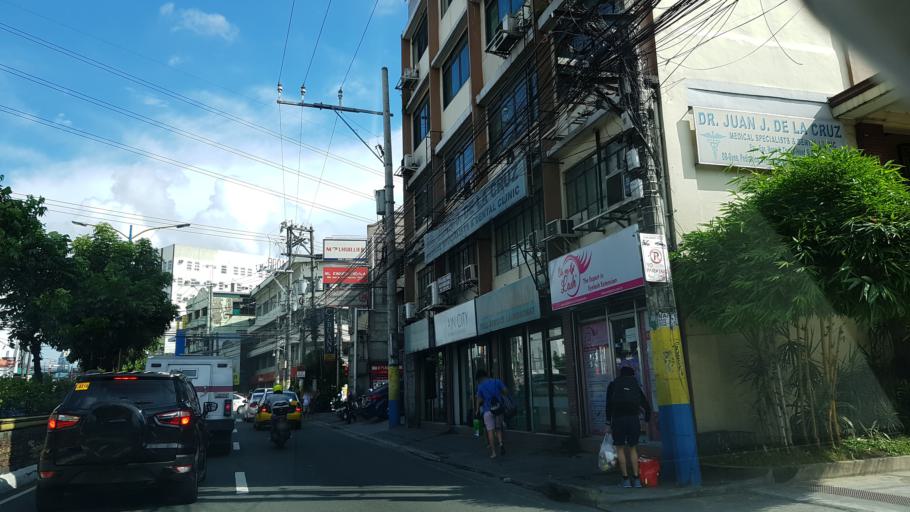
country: PH
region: Metro Manila
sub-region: Mandaluyong
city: Mandaluyong City
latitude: 14.5818
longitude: 121.0290
